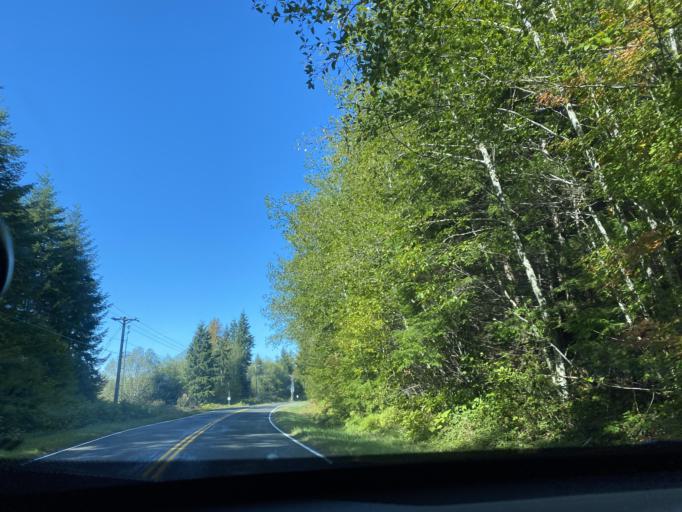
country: US
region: Washington
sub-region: Clallam County
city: Forks
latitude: 47.9471
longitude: -124.4969
